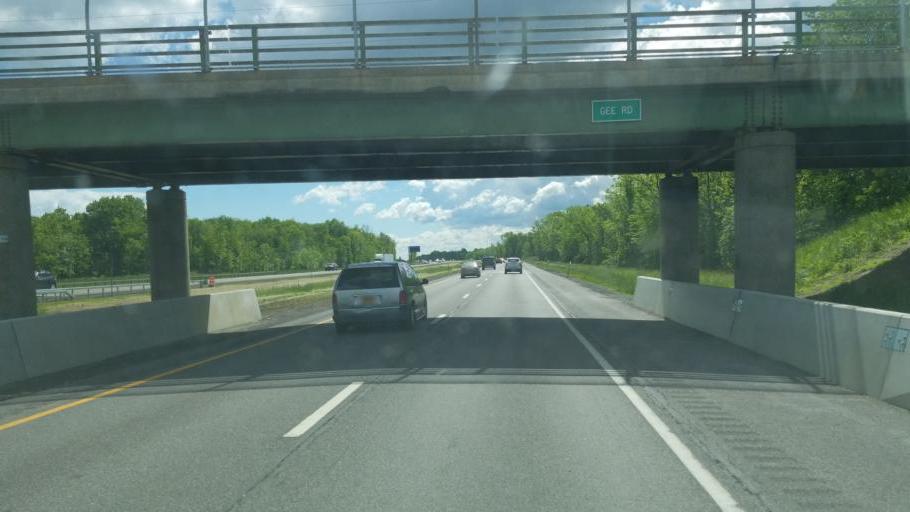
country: US
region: New York
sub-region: Madison County
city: Bolivar
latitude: 43.0944
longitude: -75.8353
